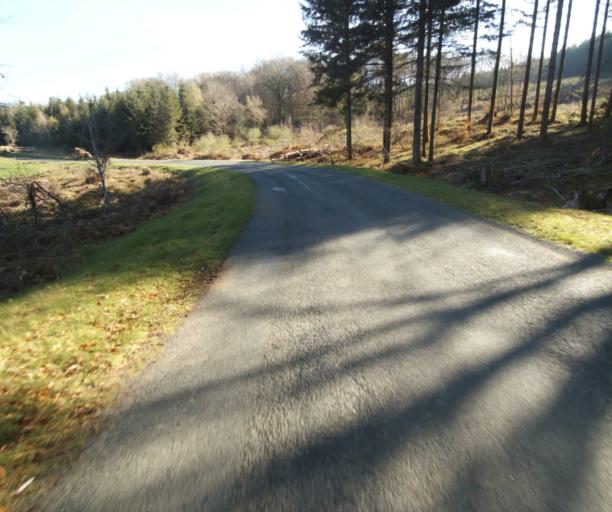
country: FR
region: Limousin
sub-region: Departement de la Correze
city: Correze
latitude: 45.2943
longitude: 1.8705
